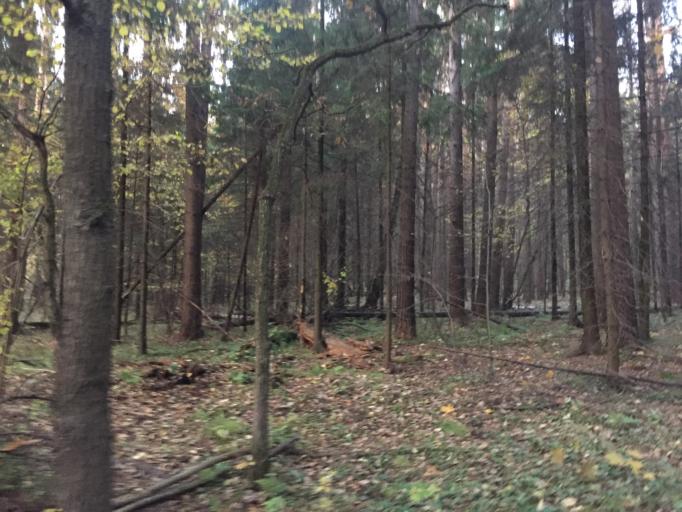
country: RU
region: Moscow
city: Gol'yanovo
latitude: 55.8573
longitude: 37.7832
